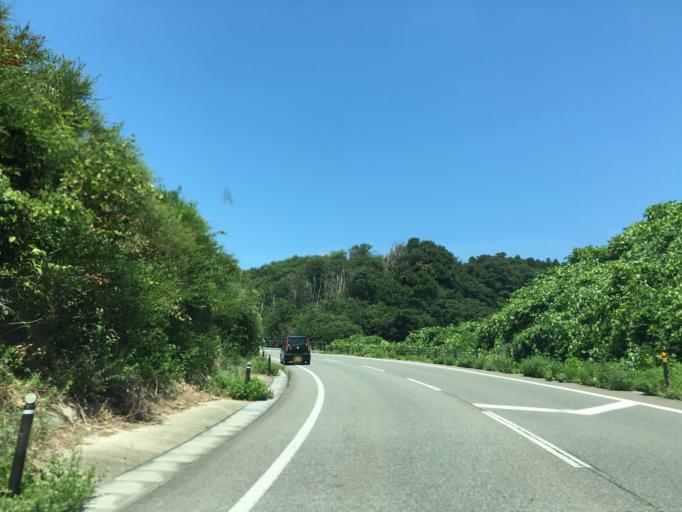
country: JP
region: Akita
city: Tenno
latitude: 39.9566
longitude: 139.7236
